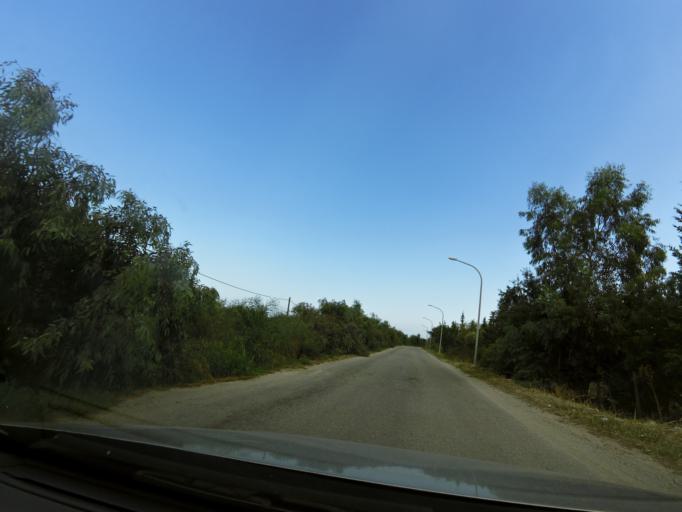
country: IT
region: Calabria
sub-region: Provincia di Reggio Calabria
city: Monasterace Marina
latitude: 38.4215
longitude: 16.5573
